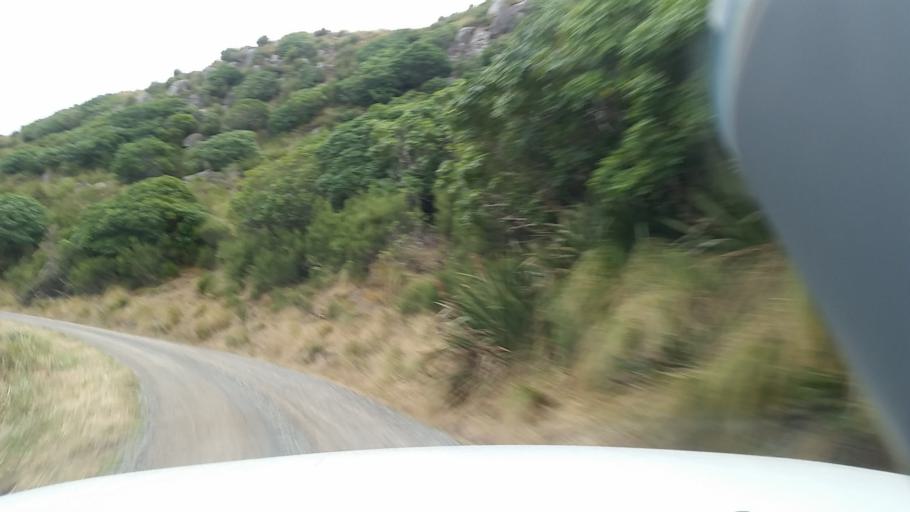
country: NZ
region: Canterbury
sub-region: Christchurch City
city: Christchurch
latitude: -43.8072
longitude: 172.8494
